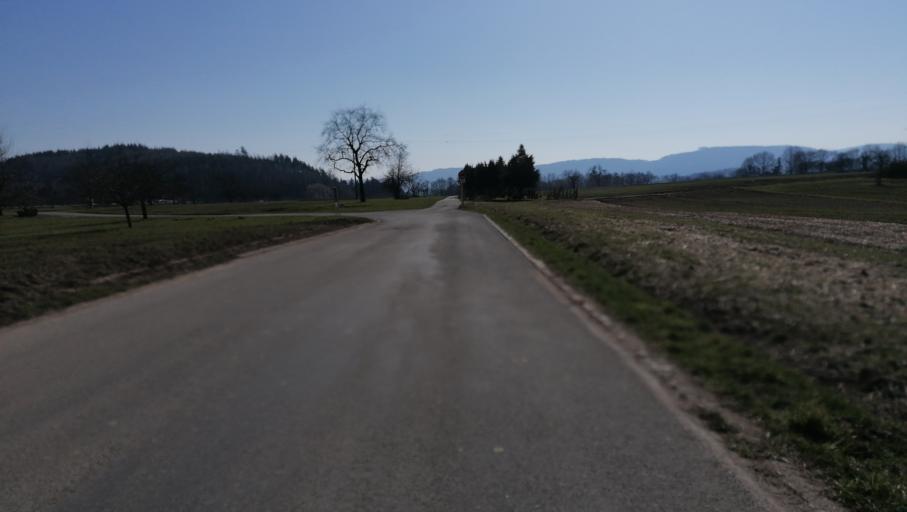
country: DE
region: Baden-Wuerttemberg
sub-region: Freiburg Region
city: Schworstadt
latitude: 47.5866
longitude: 7.9170
